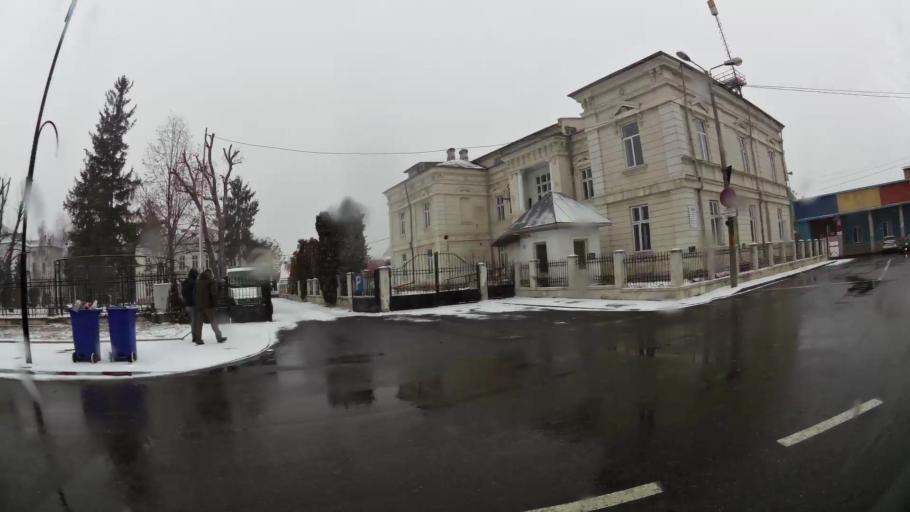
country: RO
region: Dambovita
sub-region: Municipiul Targoviste
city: Targoviste
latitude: 44.9308
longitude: 25.4614
